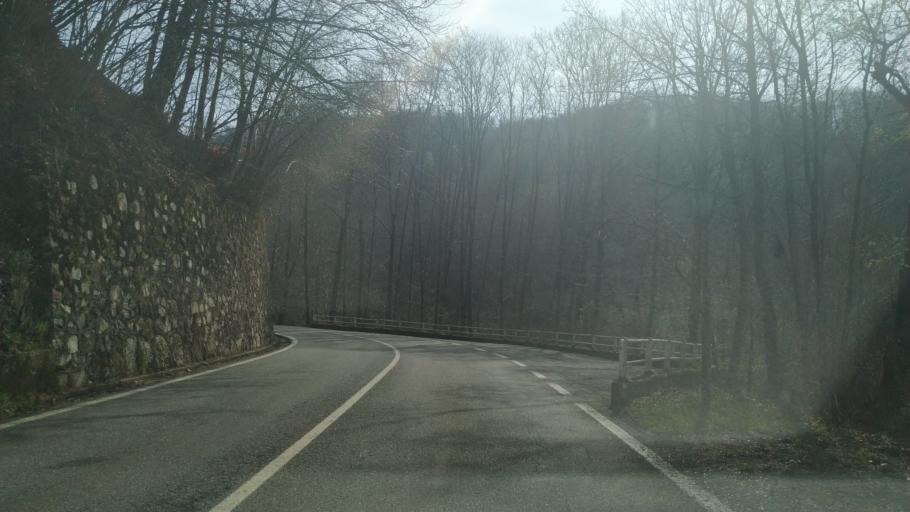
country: IT
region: Piedmont
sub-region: Provincia di Vercelli
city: Civiasco
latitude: 45.8111
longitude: 8.3094
